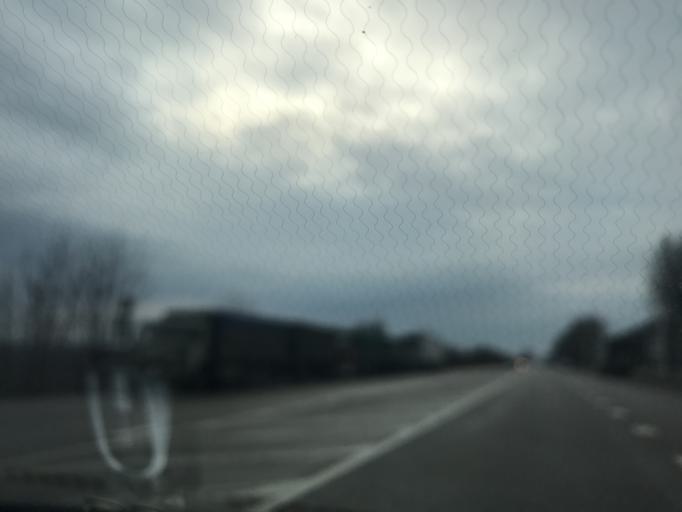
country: RU
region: Krasnodarskiy
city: Tikhoretsk
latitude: 45.8678
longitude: 40.1483
